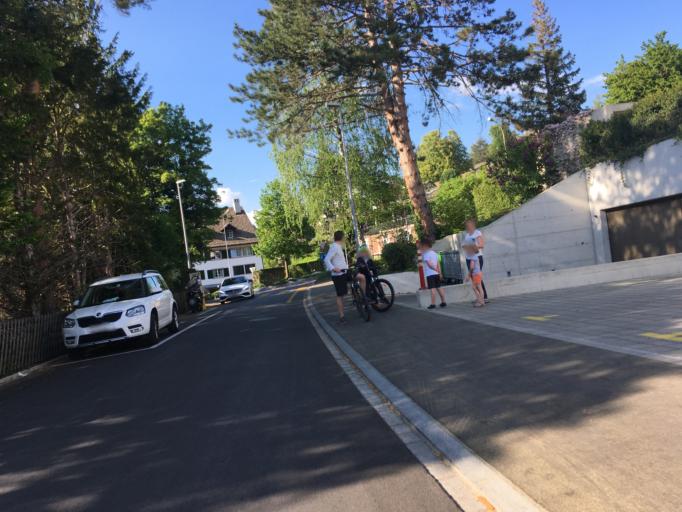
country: CH
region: Zurich
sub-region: Bezirk Meilen
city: Kuesnacht / Heslibach
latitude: 47.3111
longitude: 8.5896
